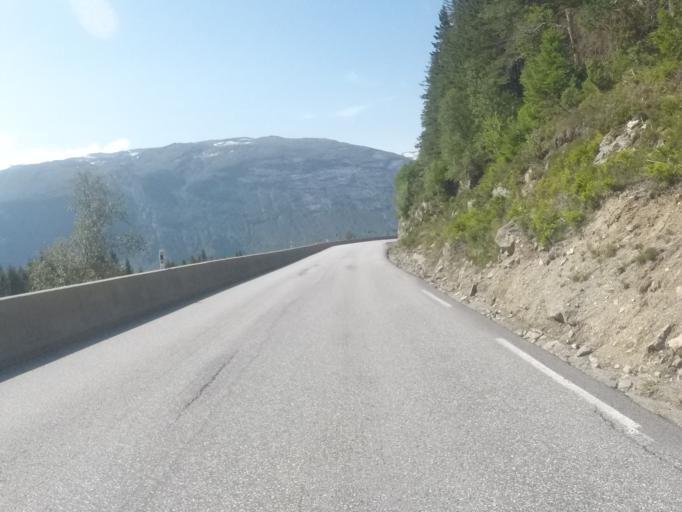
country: NO
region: Sogn og Fjordane
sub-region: Jolster
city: Skei
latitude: 61.7585
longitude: 6.4997
